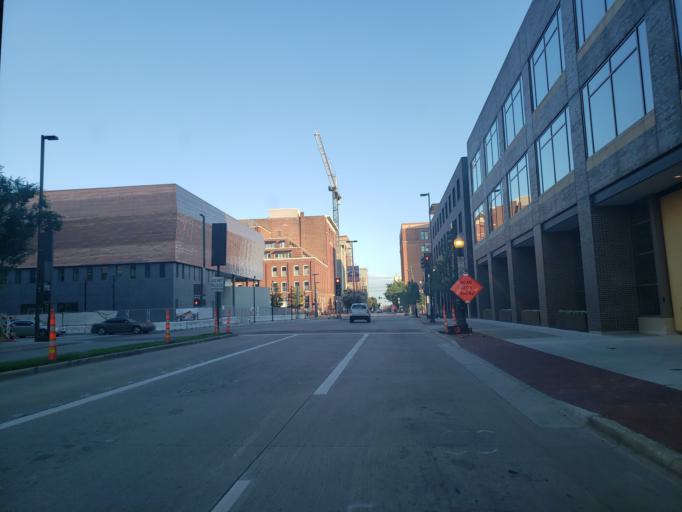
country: US
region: Texas
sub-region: Dallas County
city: Dallas
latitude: 32.7815
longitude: -96.8087
